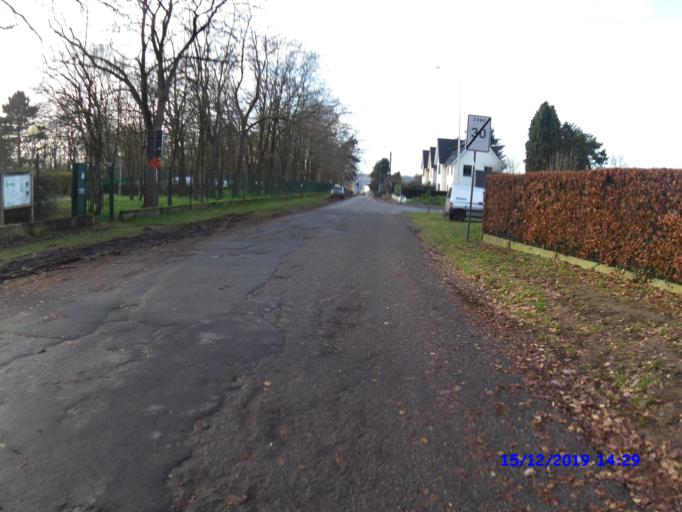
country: BE
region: Flanders
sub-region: Provincie Vlaams-Brabant
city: Beersel
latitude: 50.7280
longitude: 4.3191
